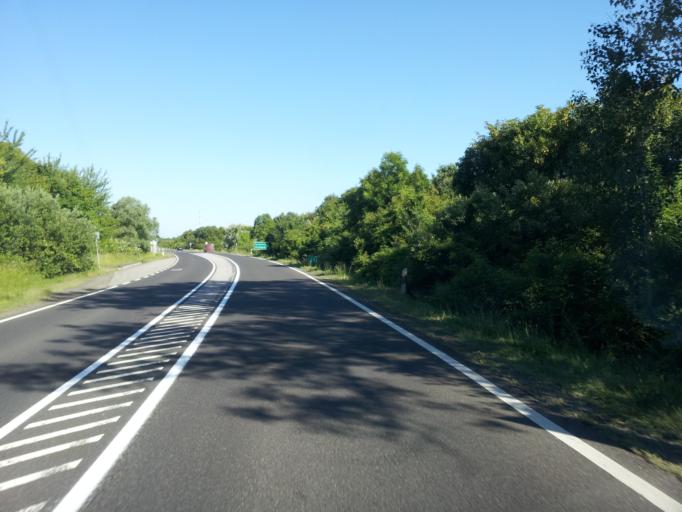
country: HU
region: Nograd
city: Nagyoroszi
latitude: 48.0466
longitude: 19.0454
